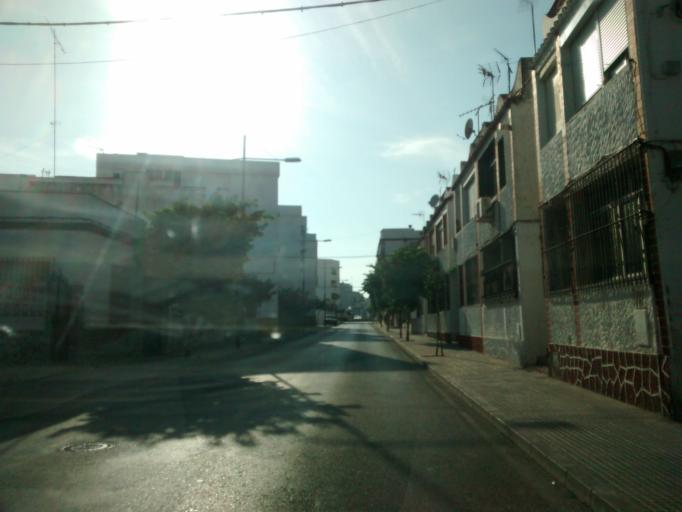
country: ES
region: Andalusia
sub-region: Provincia de Cadiz
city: Barbate de Franco
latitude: 36.1948
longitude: -5.9156
